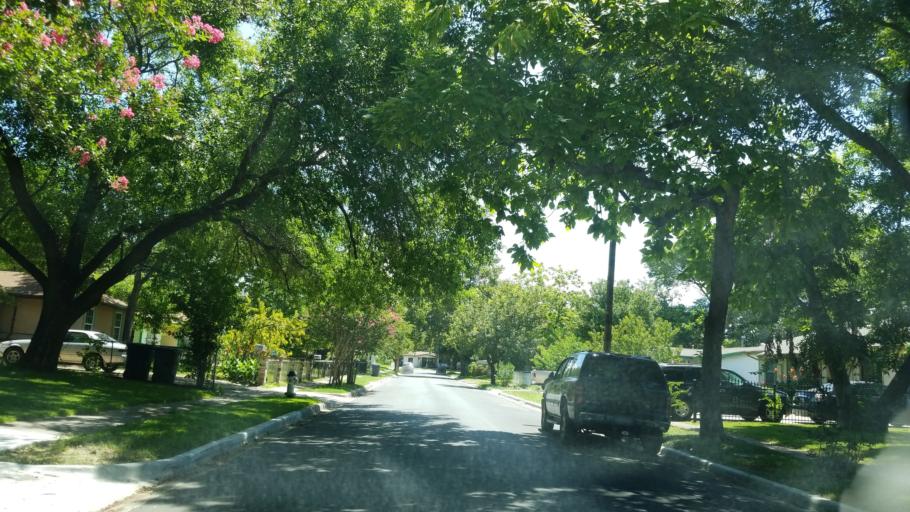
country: US
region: Texas
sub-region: Dallas County
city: Balch Springs
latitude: 32.7391
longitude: -96.6954
